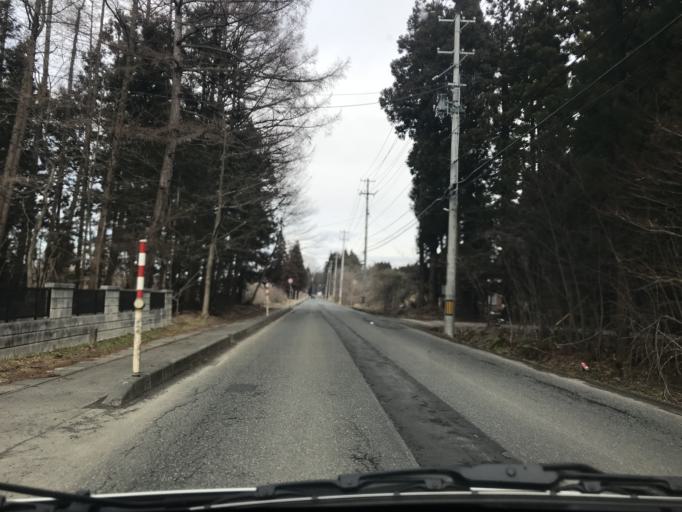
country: JP
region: Iwate
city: Kitakami
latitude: 39.3140
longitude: 141.0059
